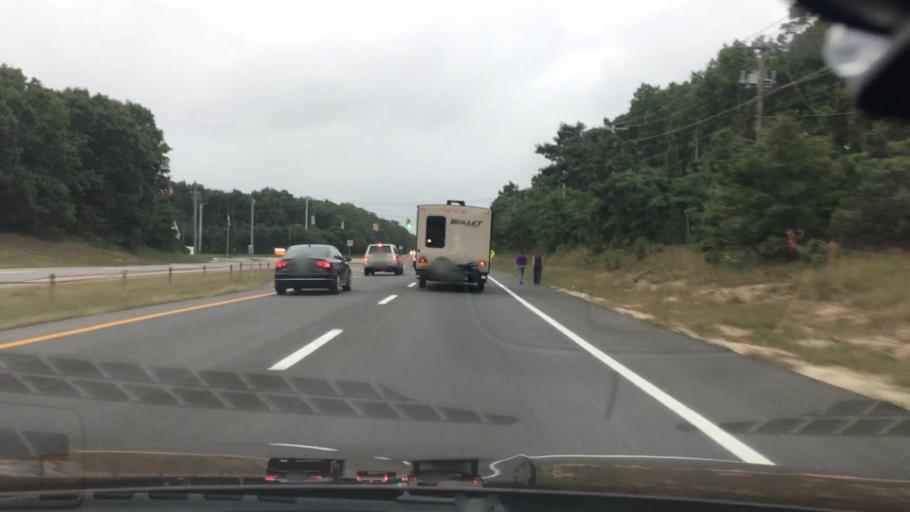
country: US
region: New York
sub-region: Suffolk County
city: Centereach
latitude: 40.8941
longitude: -73.1126
